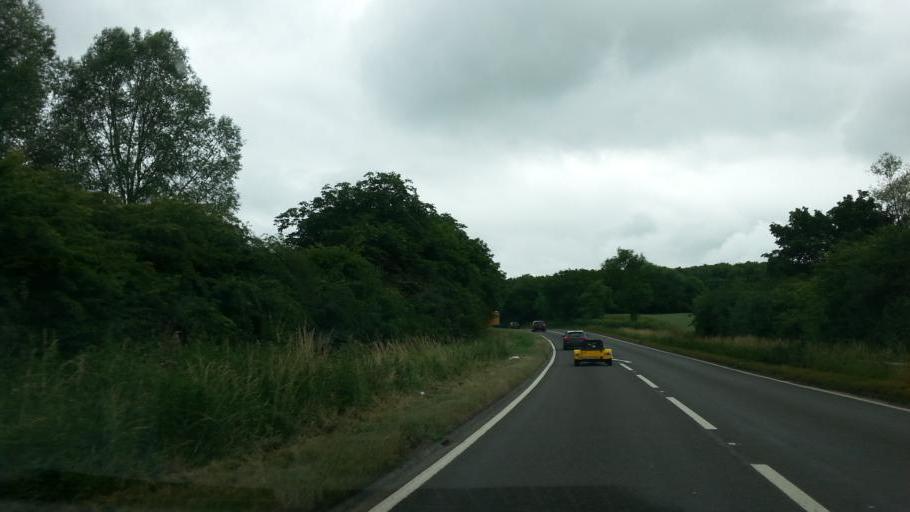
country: GB
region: England
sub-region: District of Rutland
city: Morcott
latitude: 52.5190
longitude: -0.5930
